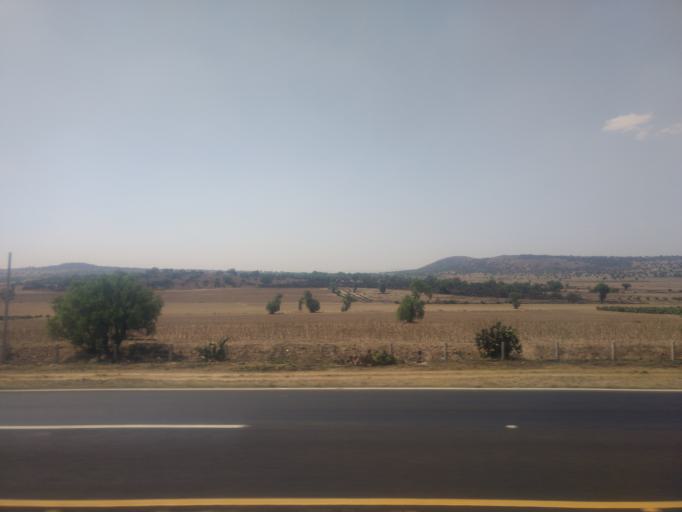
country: MX
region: Morelos
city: Nopaltepec
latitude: 19.8127
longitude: -98.7177
